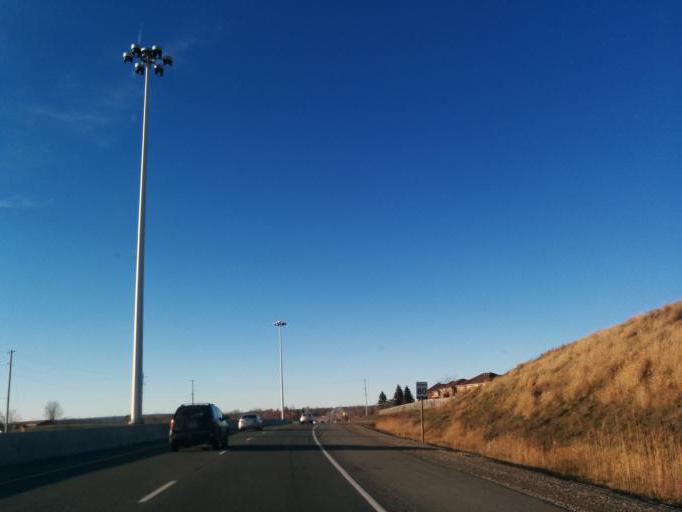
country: CA
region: Ontario
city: Brampton
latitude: 43.7424
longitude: -79.8364
